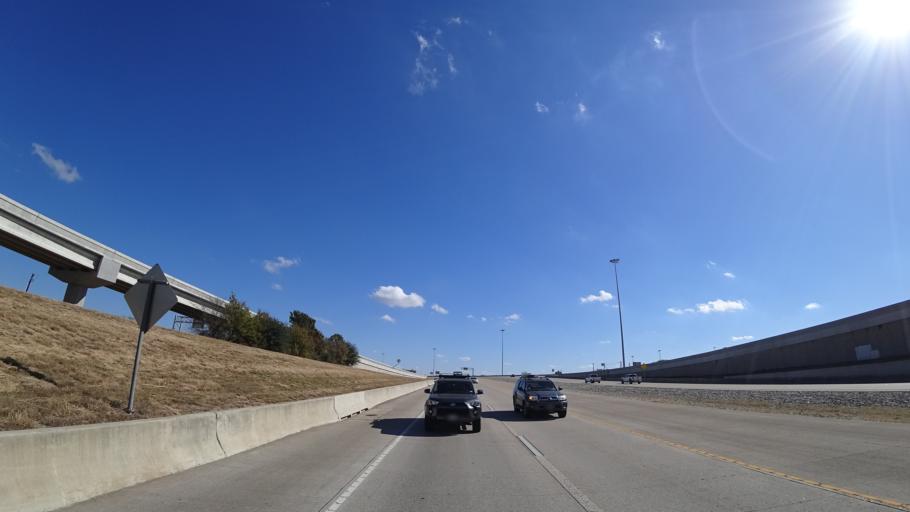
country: US
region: Texas
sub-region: Travis County
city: Rollingwood
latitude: 30.2344
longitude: -97.8222
